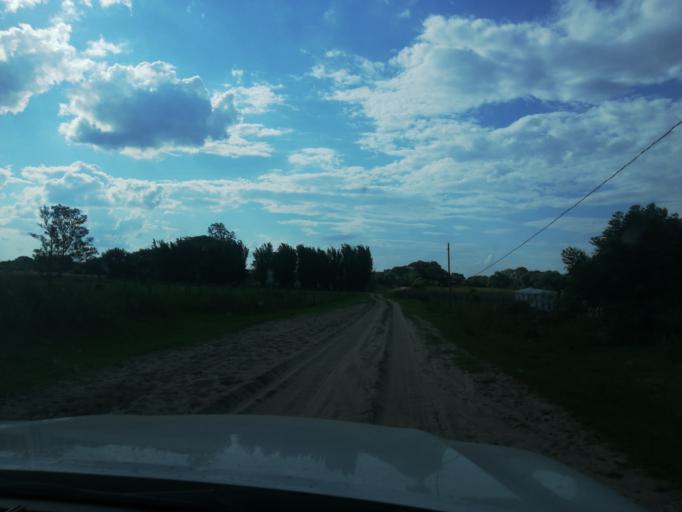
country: AR
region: Corrientes
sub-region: Departamento de San Miguel
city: San Miguel
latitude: -27.9933
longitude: -57.5747
